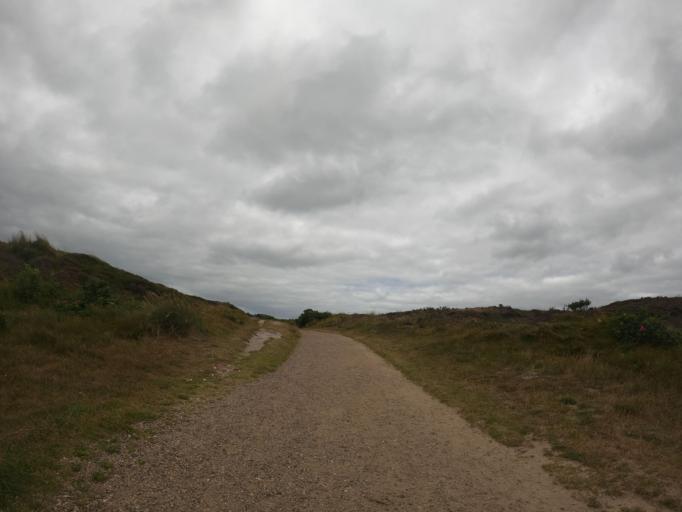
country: DE
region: Schleswig-Holstein
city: Tinnum
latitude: 54.9547
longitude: 8.3368
